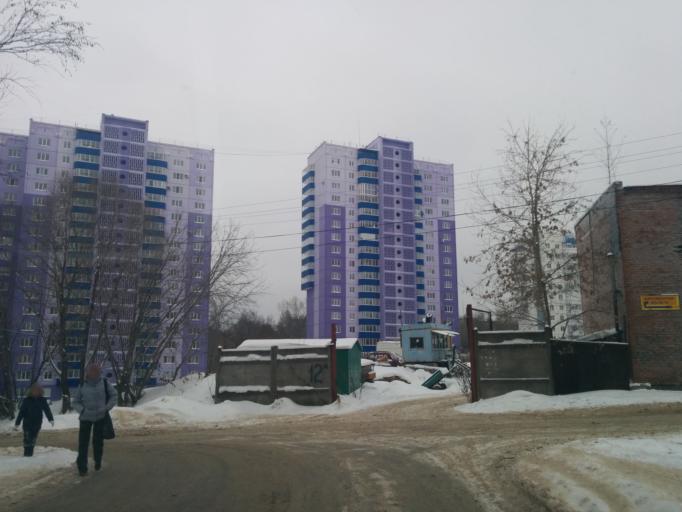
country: RU
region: Perm
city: Perm
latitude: 58.0147
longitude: 56.2978
